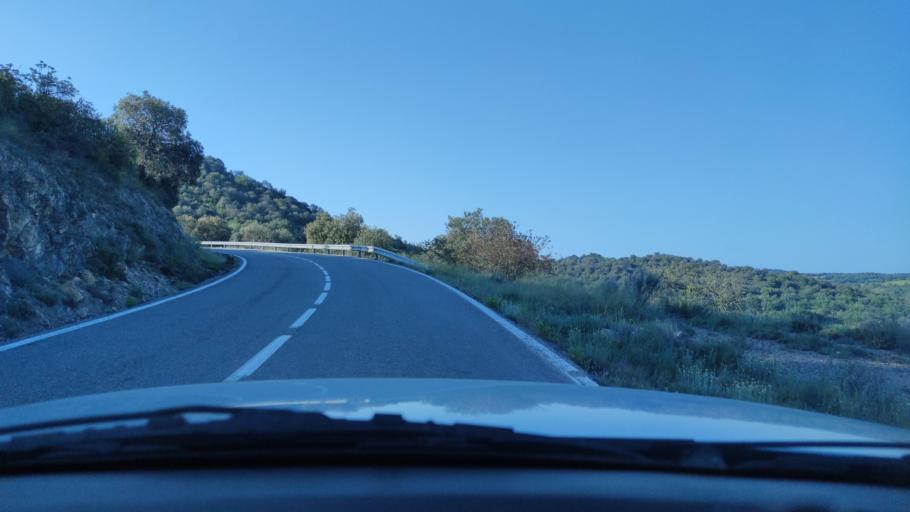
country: ES
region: Catalonia
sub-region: Provincia de Lleida
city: Artesa de Segre
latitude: 41.8826
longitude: 1.0059
